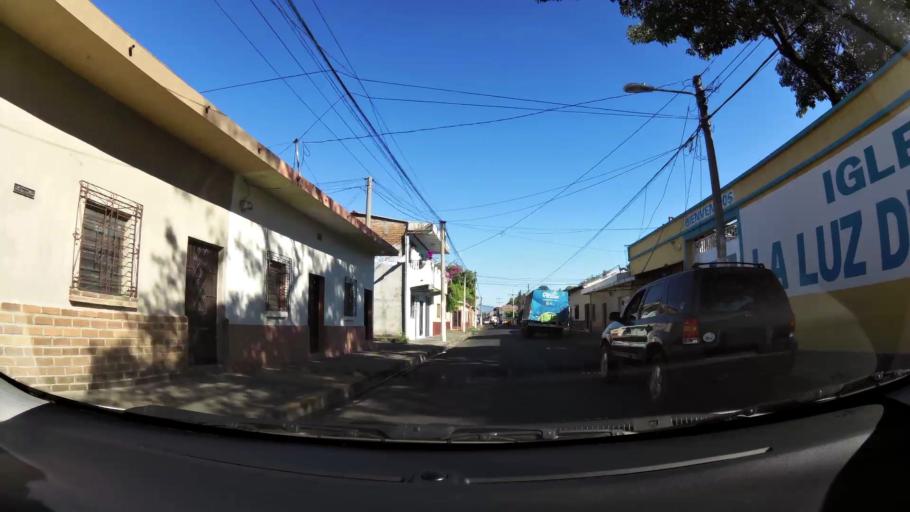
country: SV
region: San Miguel
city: San Miguel
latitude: 13.4699
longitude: -88.1770
